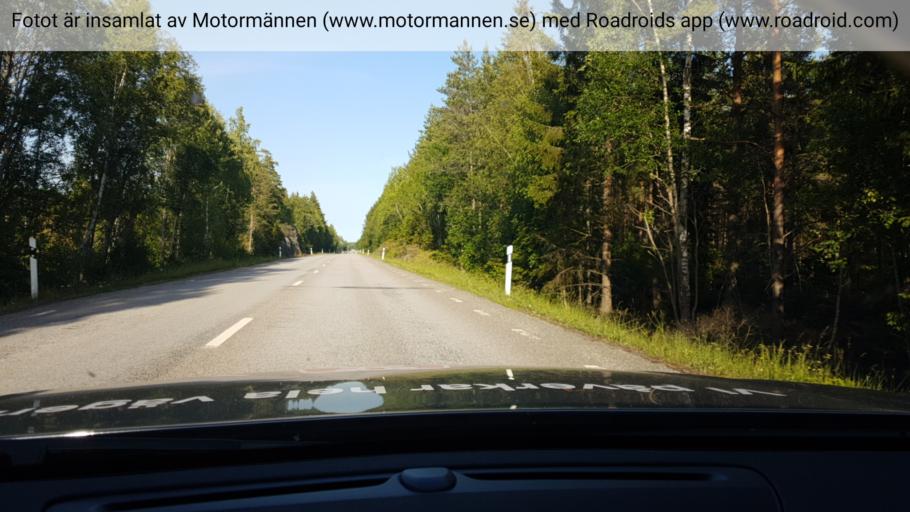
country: SE
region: Uppsala
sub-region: Osthammars Kommun
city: Gimo
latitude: 60.1650
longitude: 18.1462
